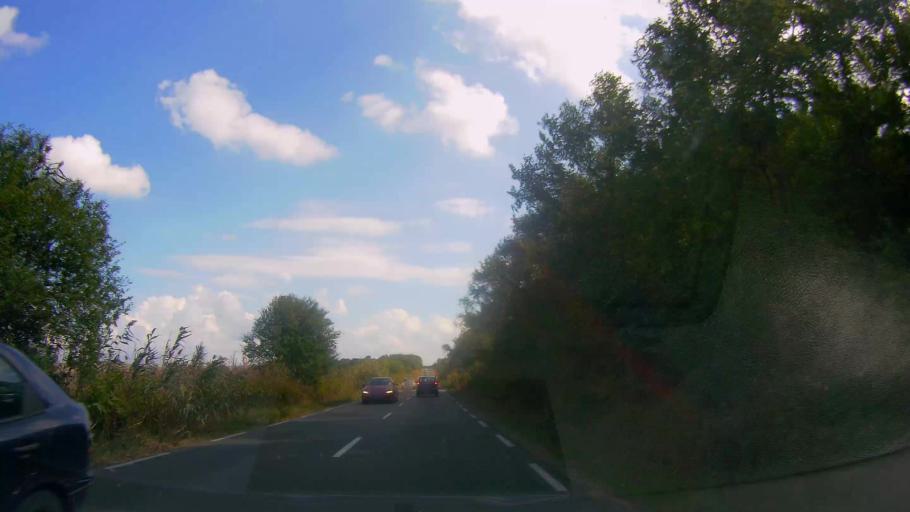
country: BG
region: Burgas
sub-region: Obshtina Kameno
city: Kameno
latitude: 42.4862
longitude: 27.3414
